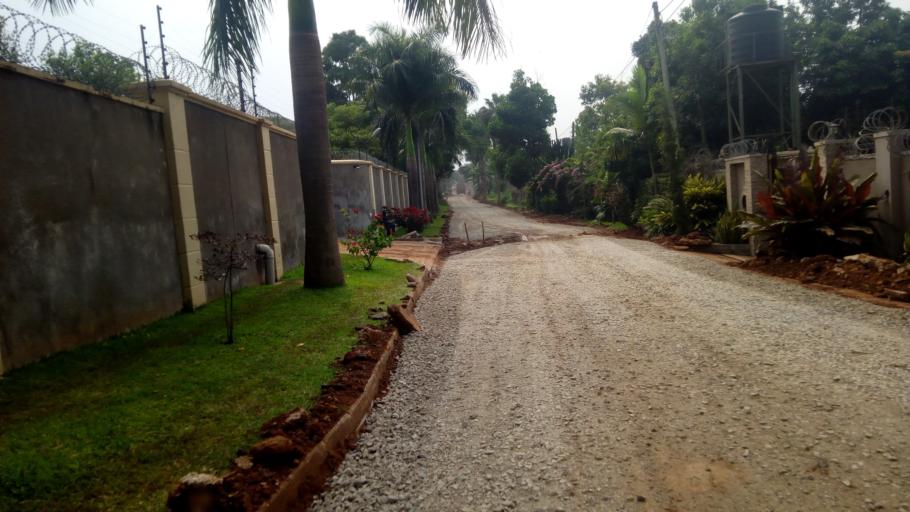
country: UG
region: Central Region
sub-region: Wakiso District
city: Kireka
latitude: 0.2905
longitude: 32.6611
